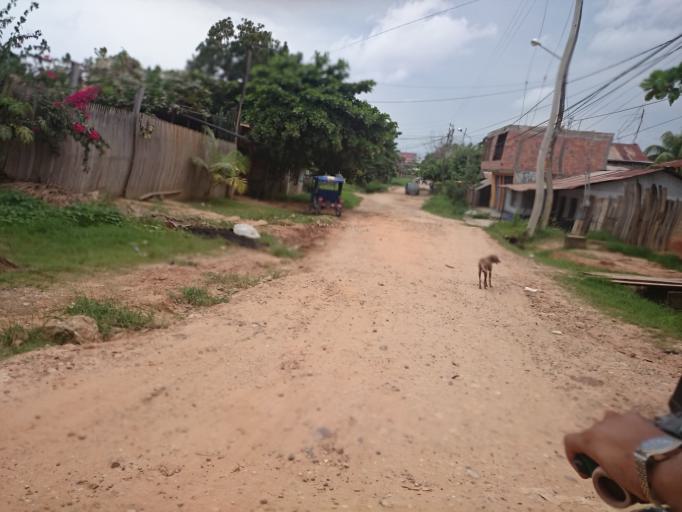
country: PE
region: Ucayali
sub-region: Provincia de Coronel Portillo
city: Pucallpa
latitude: -8.3747
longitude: -74.5536
